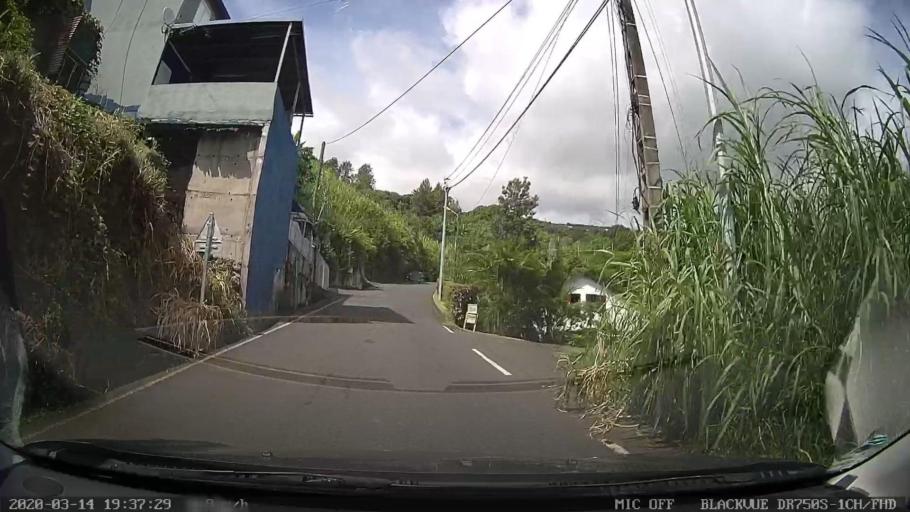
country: RE
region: Reunion
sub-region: Reunion
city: Sainte-Marie
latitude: -20.9434
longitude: 55.5223
